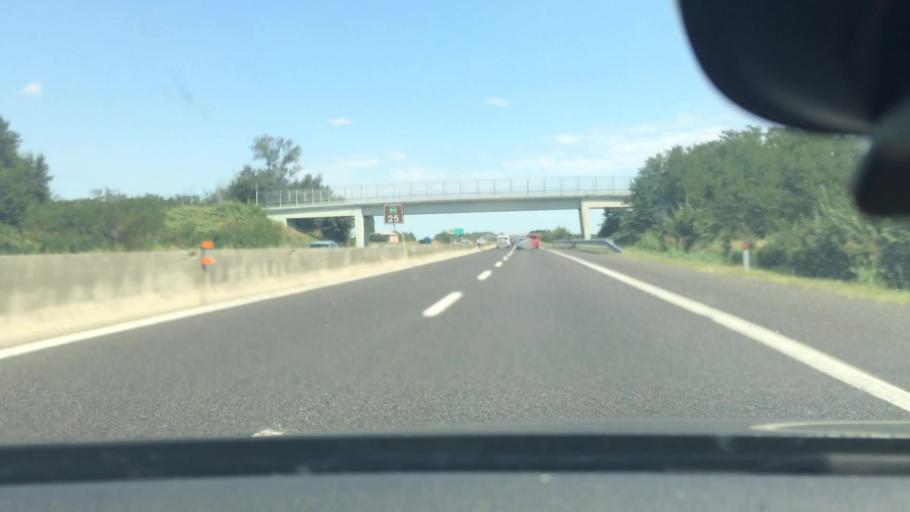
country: IT
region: Emilia-Romagna
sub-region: Provincia di Bologna
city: Malalbergo
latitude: 44.7461
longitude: 11.5267
